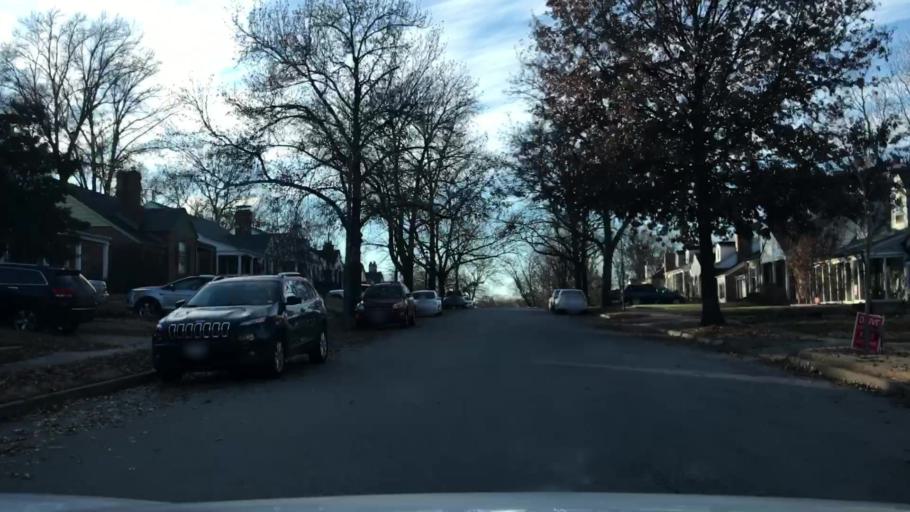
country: US
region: Missouri
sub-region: Saint Louis County
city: Brentwood
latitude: 38.6188
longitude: -90.3430
